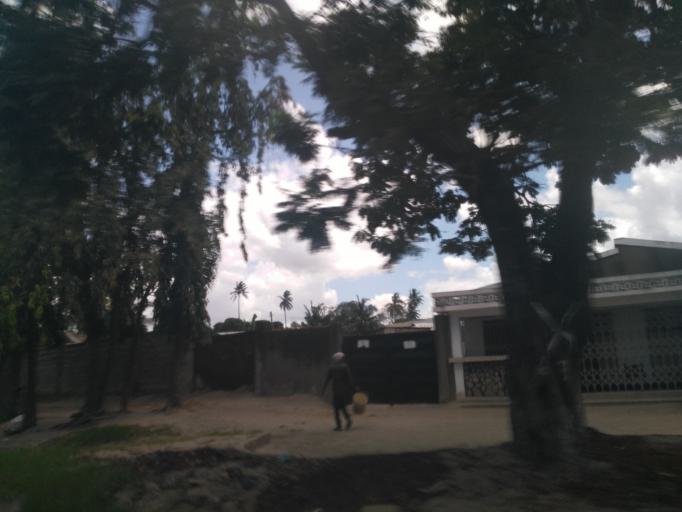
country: TZ
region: Dar es Salaam
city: Dar es Salaam
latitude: -6.8670
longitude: 39.2729
